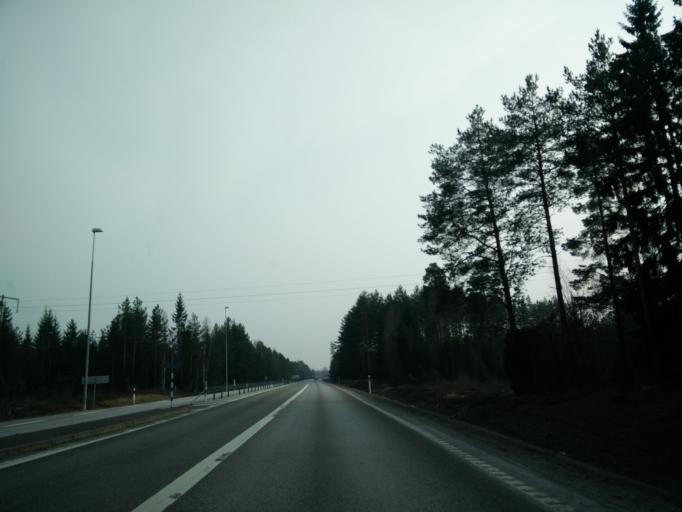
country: SE
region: Vaermland
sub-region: Forshaga Kommun
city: Forshaga
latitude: 59.4551
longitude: 13.4166
